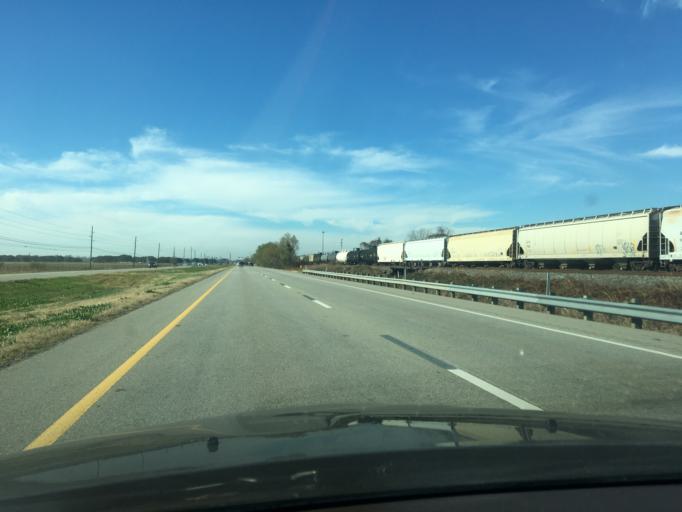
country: US
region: Texas
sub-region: Fort Bend County
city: New Territory
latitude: 29.5994
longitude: -95.7078
